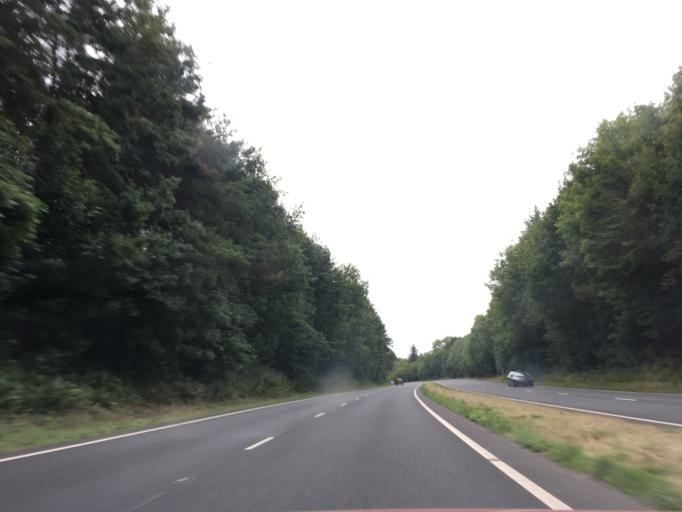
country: GB
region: Wales
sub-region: Sir Powys
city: Brecon
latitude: 51.9370
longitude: -3.3695
